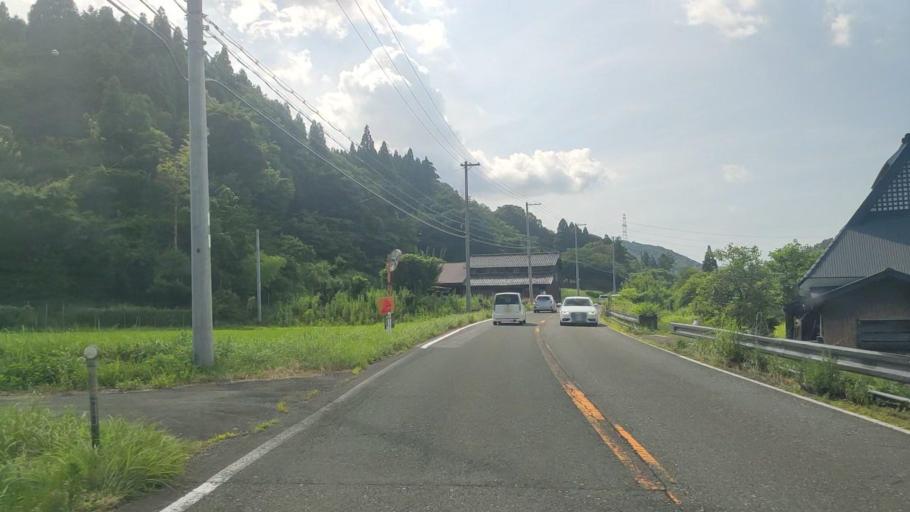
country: JP
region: Fukui
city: Tsuruga
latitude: 35.5524
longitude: 136.1420
